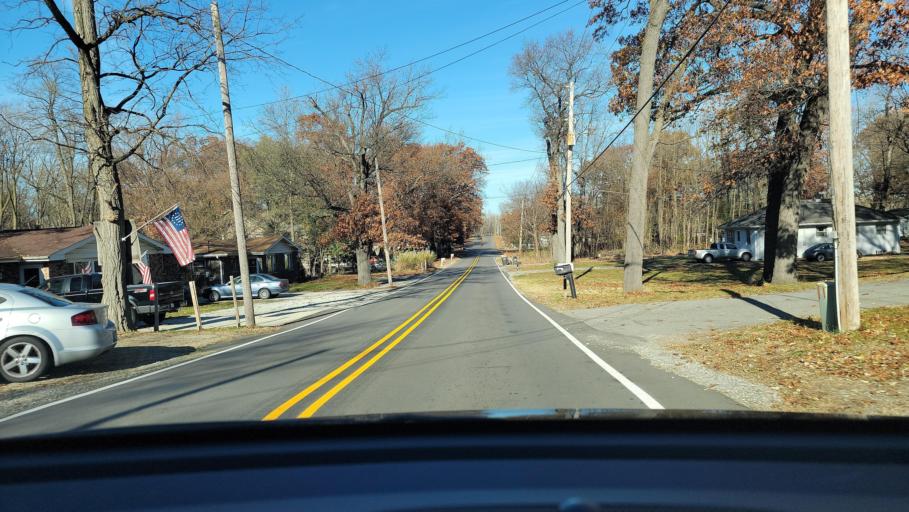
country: US
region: Indiana
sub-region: Porter County
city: Portage
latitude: 41.5861
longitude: -87.1978
